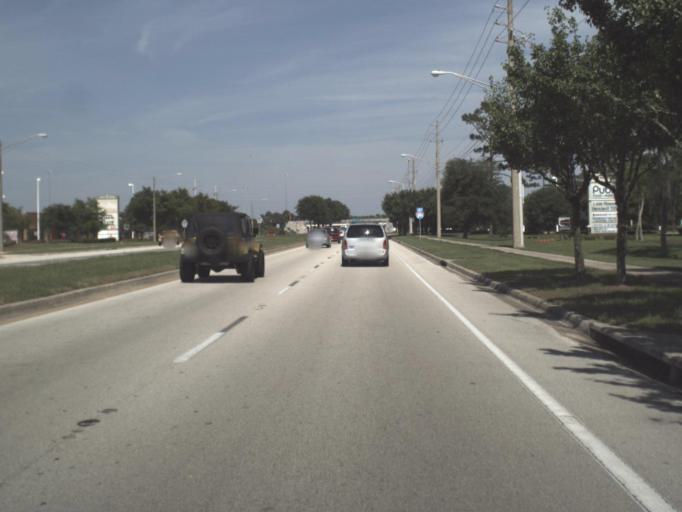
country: US
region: Florida
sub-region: Saint Johns County
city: Ponte Vedra Beach
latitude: 30.2157
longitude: -81.5195
